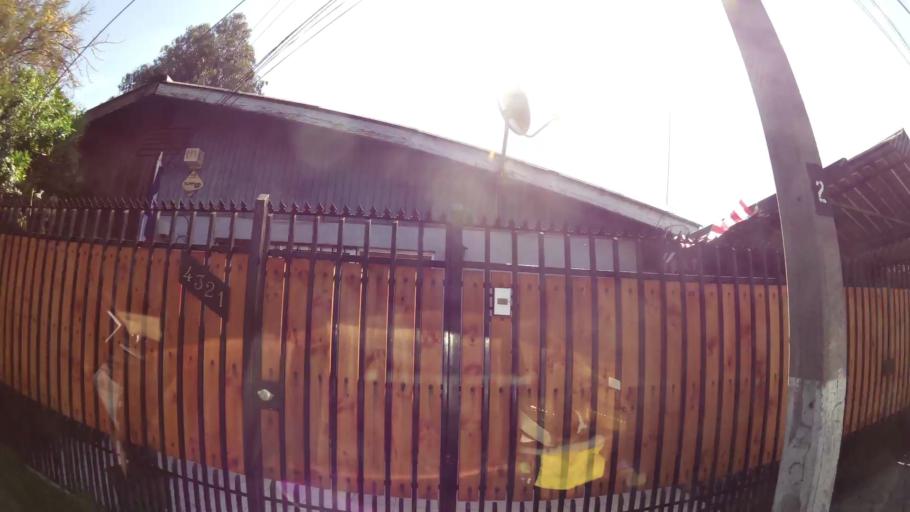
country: CL
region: Santiago Metropolitan
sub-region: Provincia de Santiago
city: Villa Presidente Frei, Nunoa, Santiago, Chile
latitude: -33.4983
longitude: -70.5804
